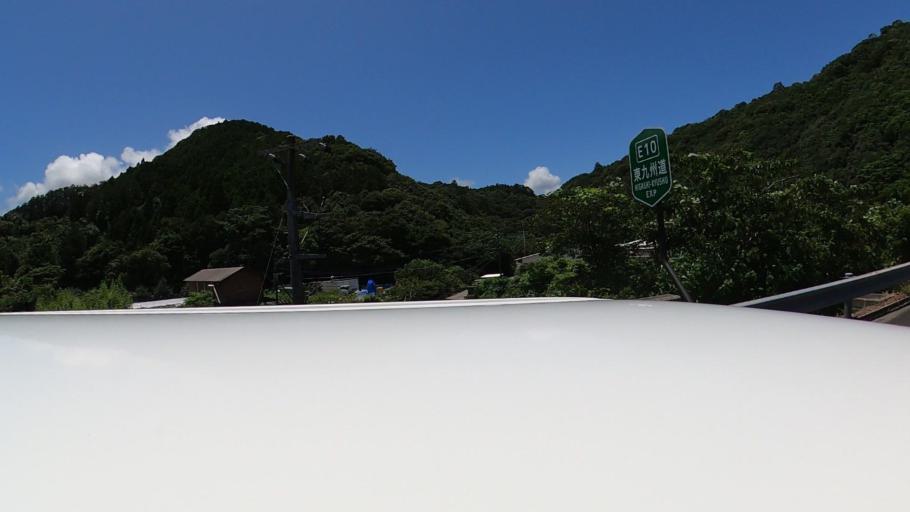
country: JP
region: Miyazaki
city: Nobeoka
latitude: 32.5313
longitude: 131.6644
